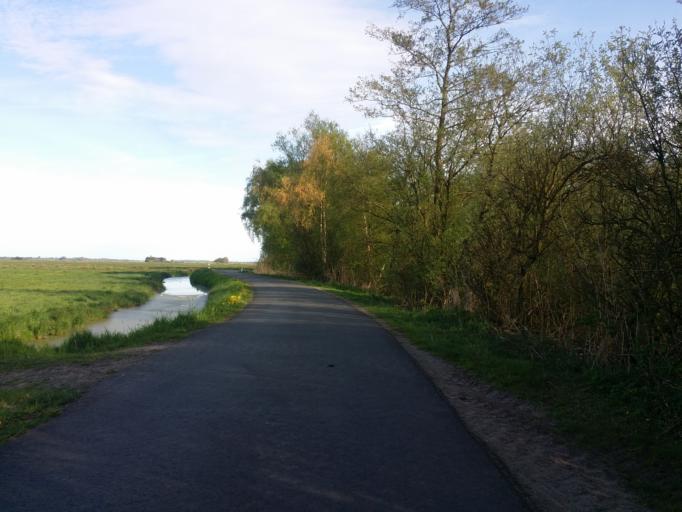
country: DE
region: Lower Saxony
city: Ritterhude
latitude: 53.1546
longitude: 8.7816
